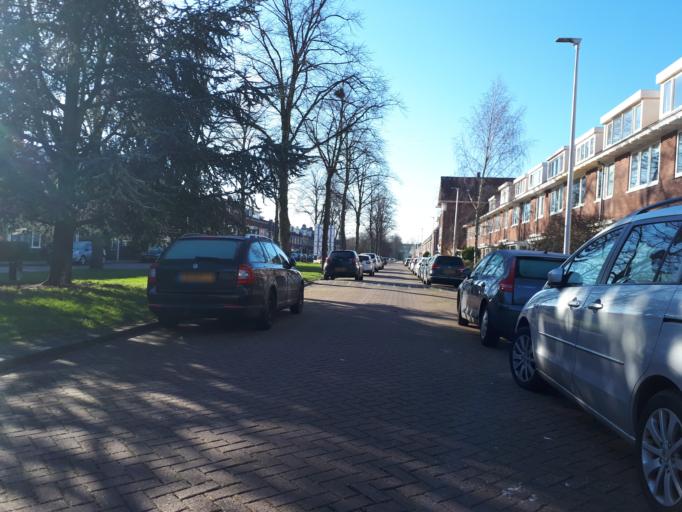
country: NL
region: Utrecht
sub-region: Gemeente Utrecht
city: Lunetten
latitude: 52.0640
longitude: 5.1176
